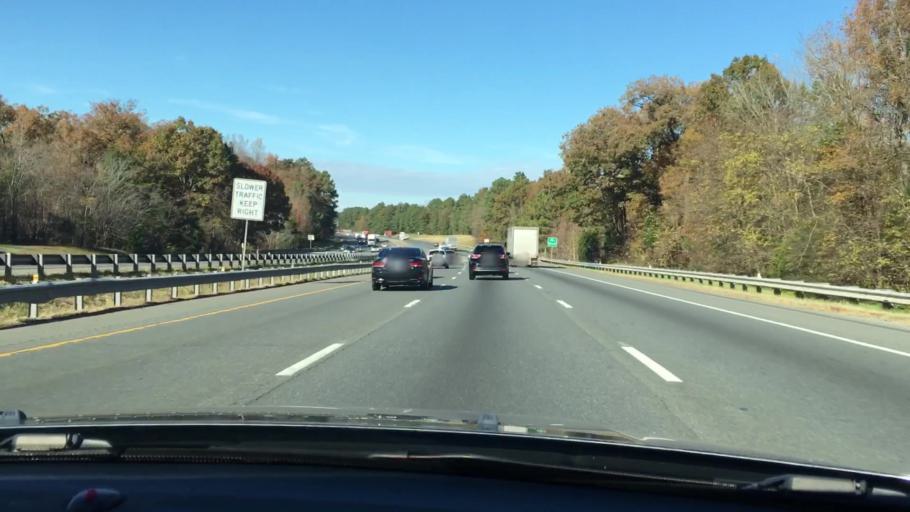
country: US
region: Virginia
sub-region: Spotsylvania County
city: Spotsylvania Courthouse
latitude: 38.1448
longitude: -77.5060
